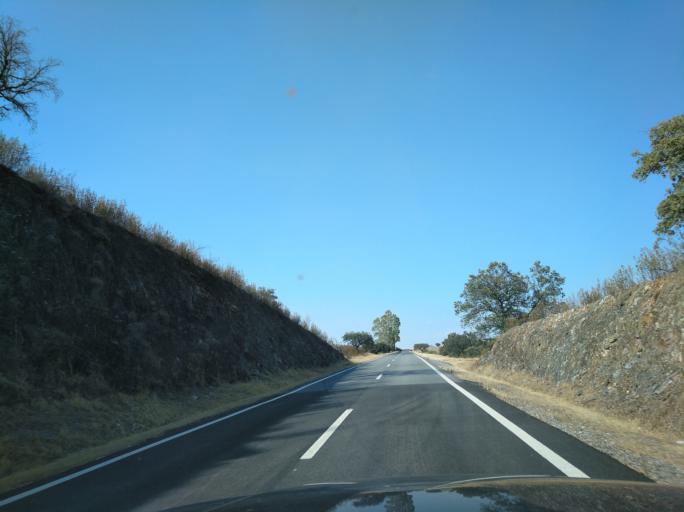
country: ES
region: Extremadura
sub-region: Provincia de Badajoz
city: Valencia del Mombuey
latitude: 38.1548
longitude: -7.2342
